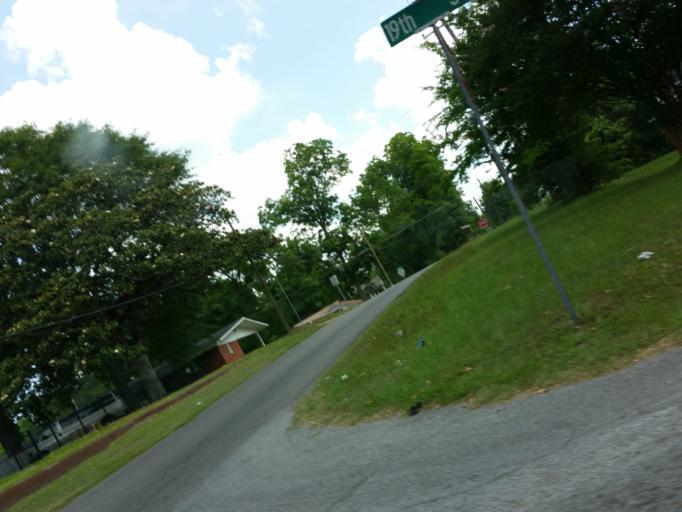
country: US
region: Mississippi
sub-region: Lauderdale County
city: Meridian
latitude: 32.3774
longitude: -88.7205
